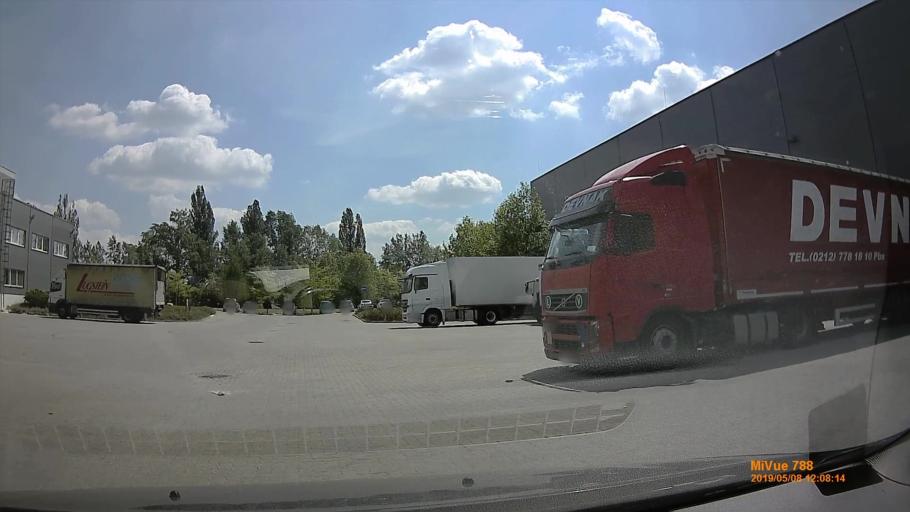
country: HU
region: Budapest
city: Budapest XV. keruelet
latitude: 47.6048
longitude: 19.1050
